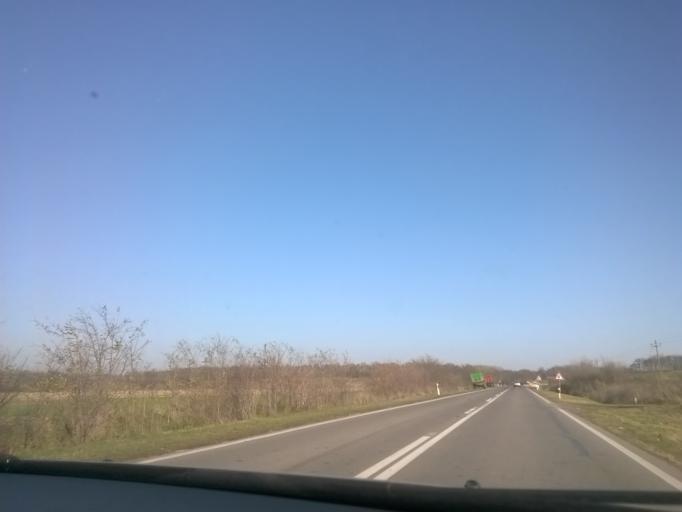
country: RS
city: Vlajkovac
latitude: 45.0668
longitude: 21.1897
